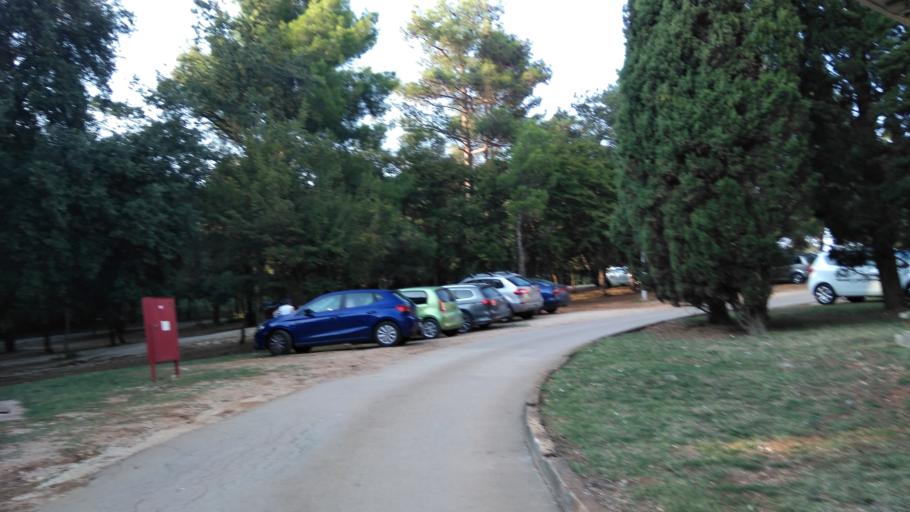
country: HR
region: Istarska
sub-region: Grad Porec
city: Porec
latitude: 45.1966
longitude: 13.5831
